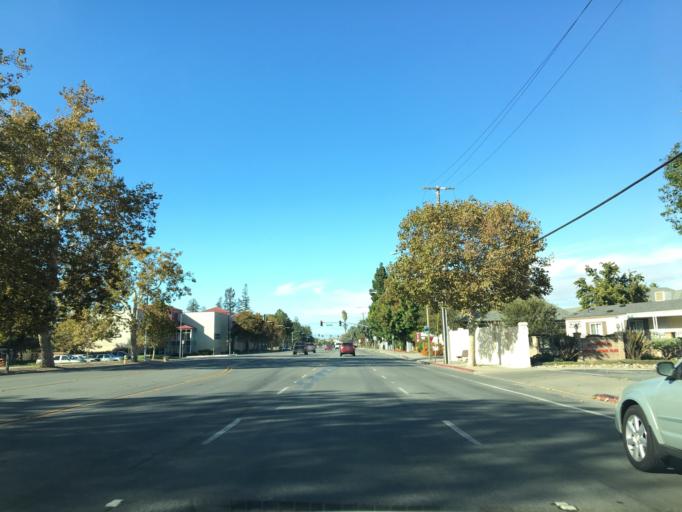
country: US
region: California
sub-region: Santa Clara County
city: San Jose
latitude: 37.3708
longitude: -121.8931
